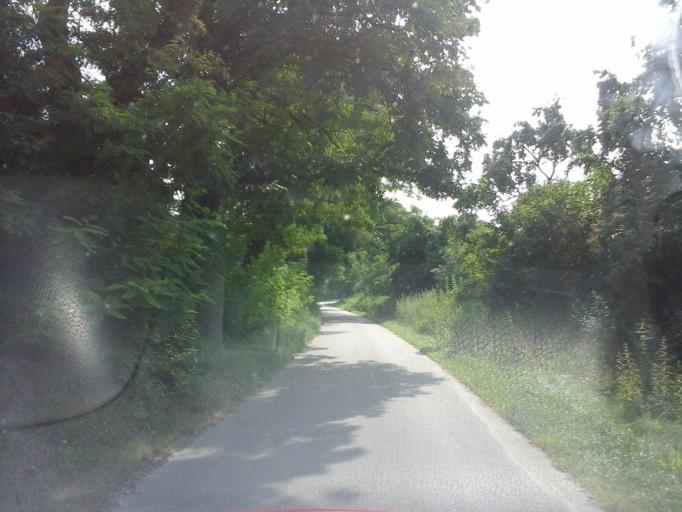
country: PL
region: West Pomeranian Voivodeship
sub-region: Powiat mysliborski
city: Barlinek
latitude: 53.0458
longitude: 15.2381
